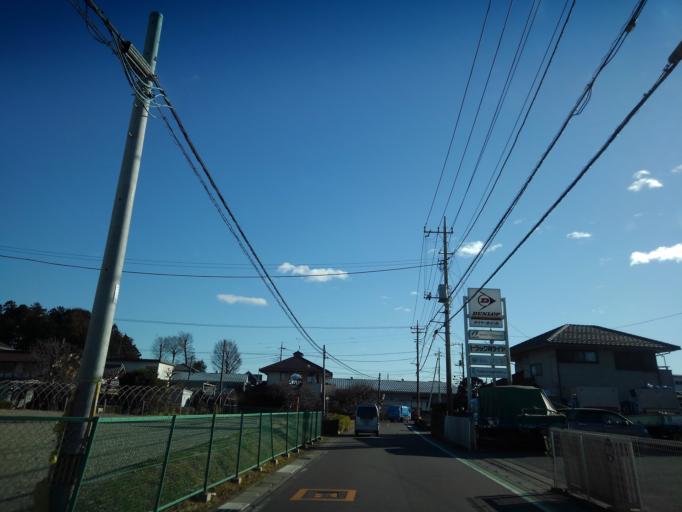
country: JP
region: Saitama
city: Oi
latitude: 35.8067
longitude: 139.5186
